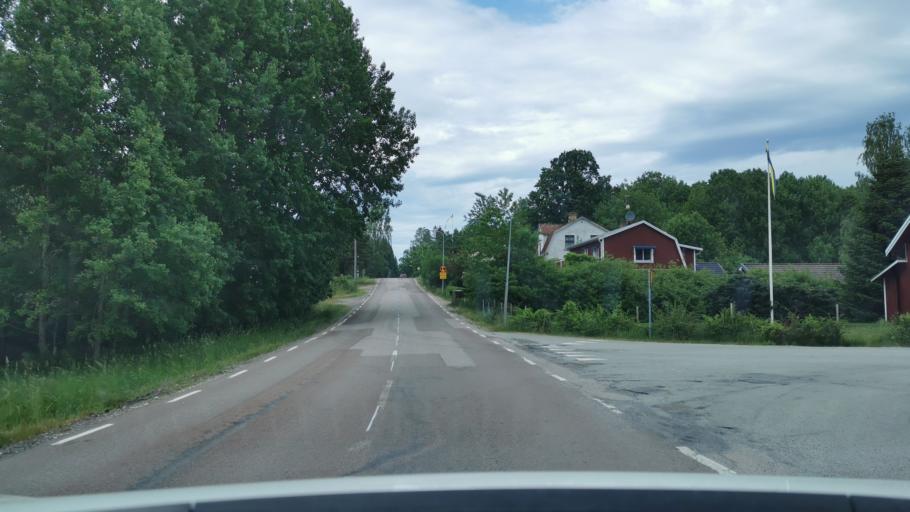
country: SE
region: Vaestra Goetaland
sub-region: Melleruds Kommun
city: Mellerud
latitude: 58.8260
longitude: 12.4138
